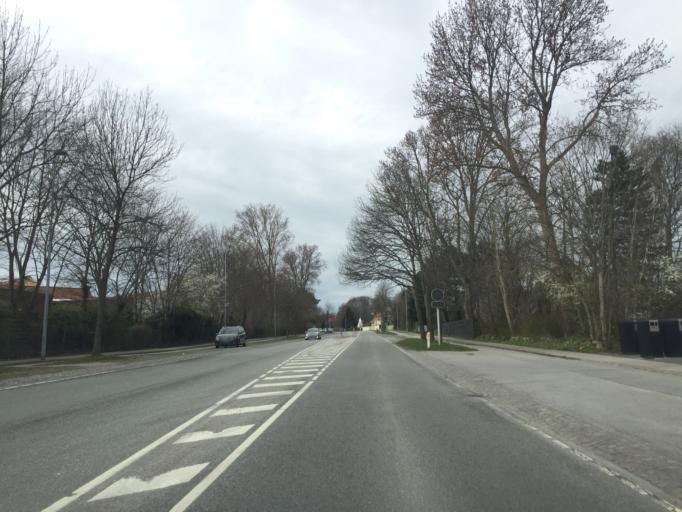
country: DK
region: Capital Region
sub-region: Gladsaxe Municipality
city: Buddinge
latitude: 55.7650
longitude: 12.4533
